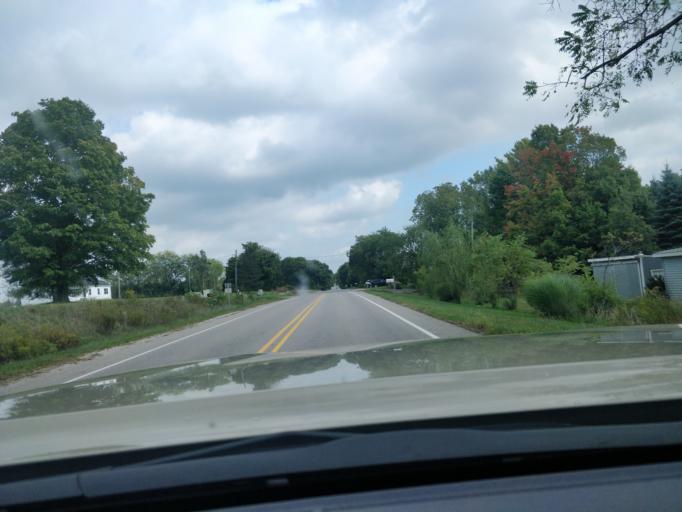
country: US
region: Michigan
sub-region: Kent County
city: Lowell
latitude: 42.8859
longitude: -85.3128
